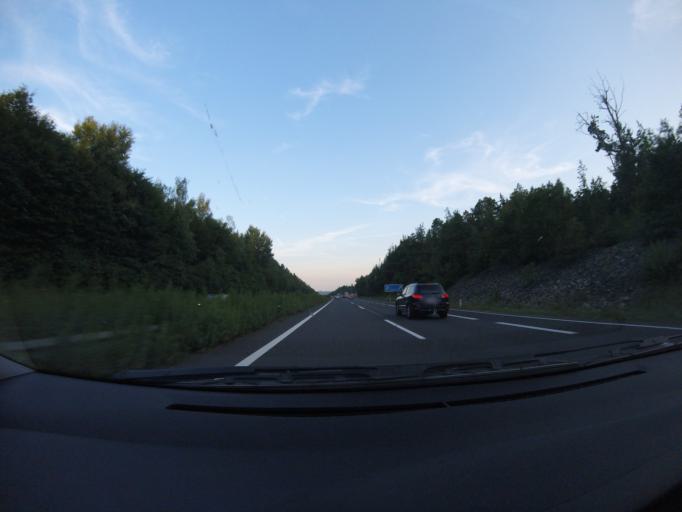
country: AT
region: Styria
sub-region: Politischer Bezirk Hartberg-Fuerstenfeld
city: Hainersdorf
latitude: 47.1230
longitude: 15.9842
